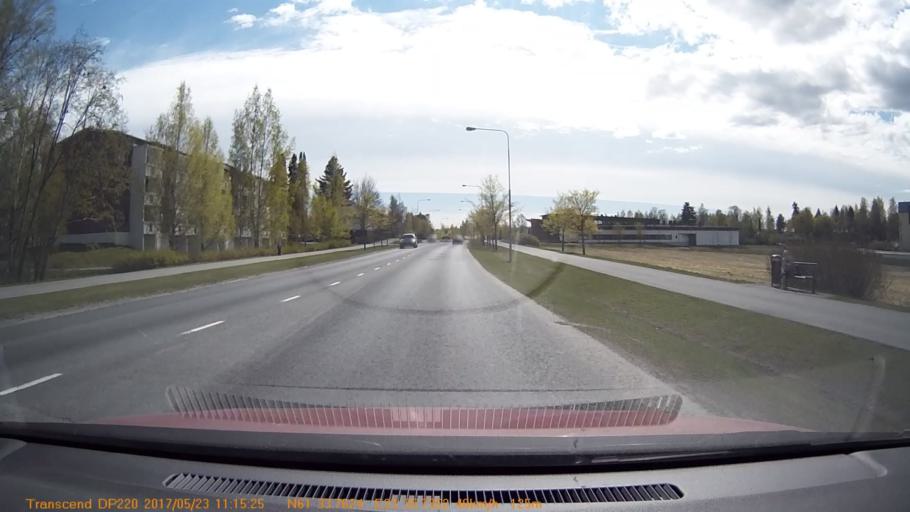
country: FI
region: Pirkanmaa
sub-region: Tampere
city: Yloejaervi
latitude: 61.5628
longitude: 23.5956
